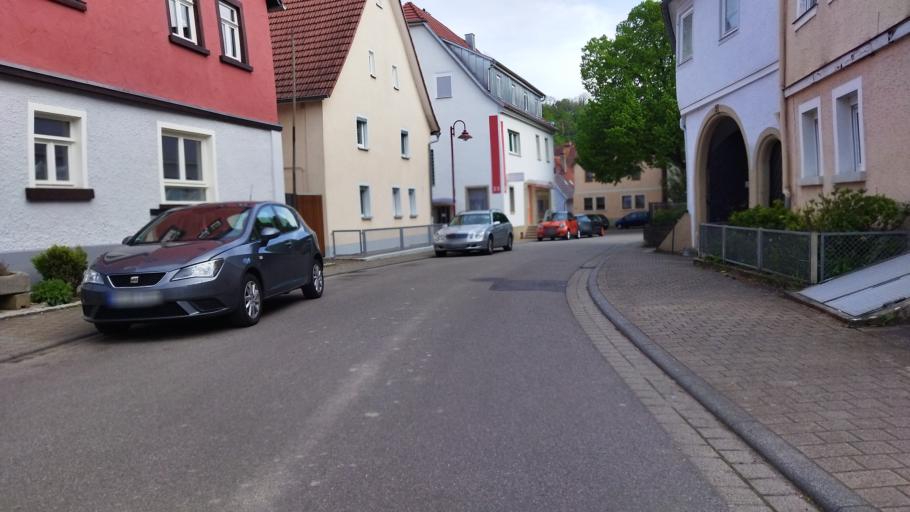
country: DE
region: Baden-Wuerttemberg
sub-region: Karlsruhe Region
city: Hassmersheim
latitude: 49.3001
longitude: 9.1504
